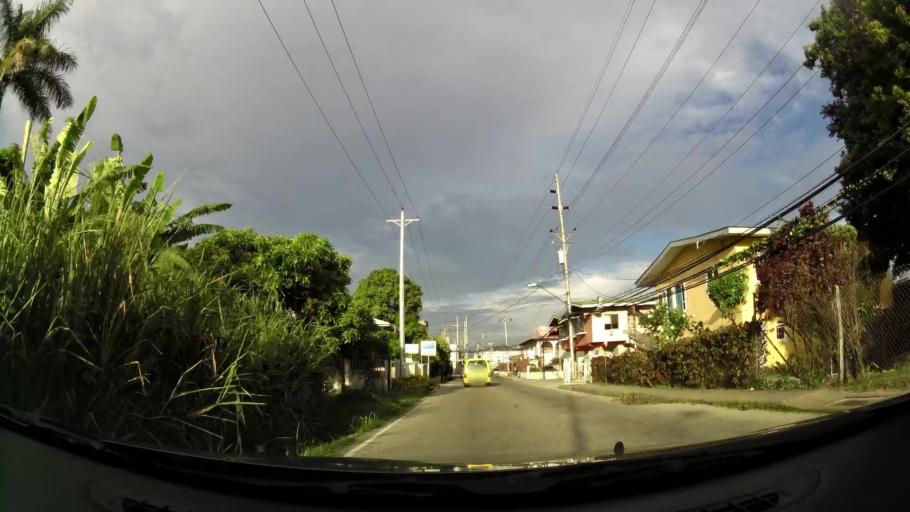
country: TT
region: Tunapuna/Piarco
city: Tunapuna
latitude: 10.6384
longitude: -61.4022
